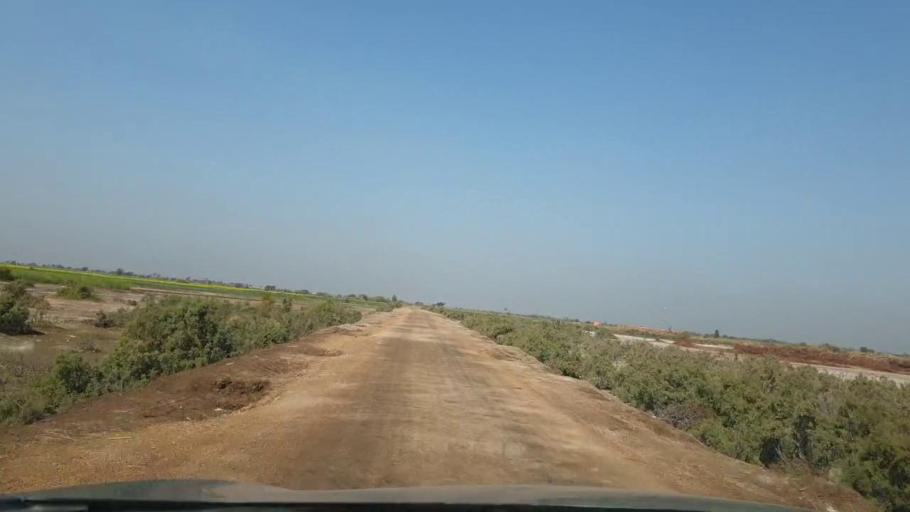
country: PK
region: Sindh
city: Berani
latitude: 25.7044
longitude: 68.8662
